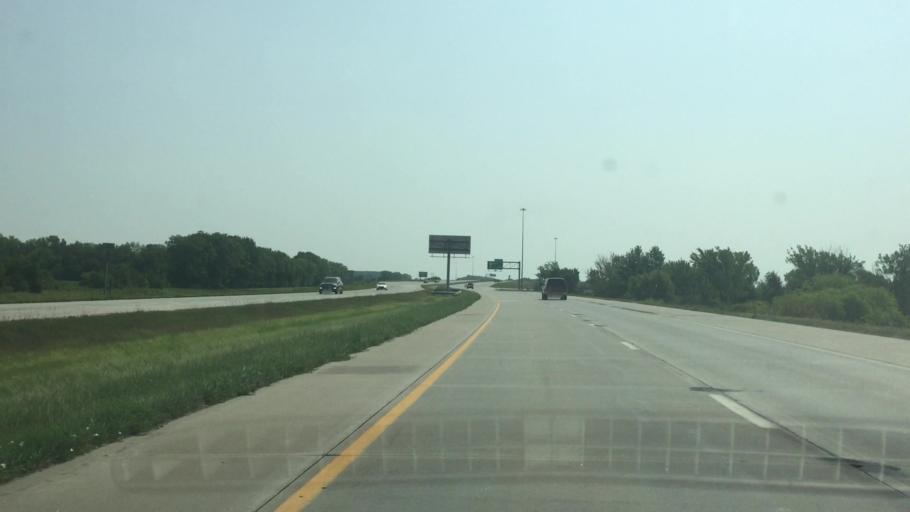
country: US
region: Kansas
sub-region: Lyon County
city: Emporia
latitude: 38.4116
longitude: -96.1478
